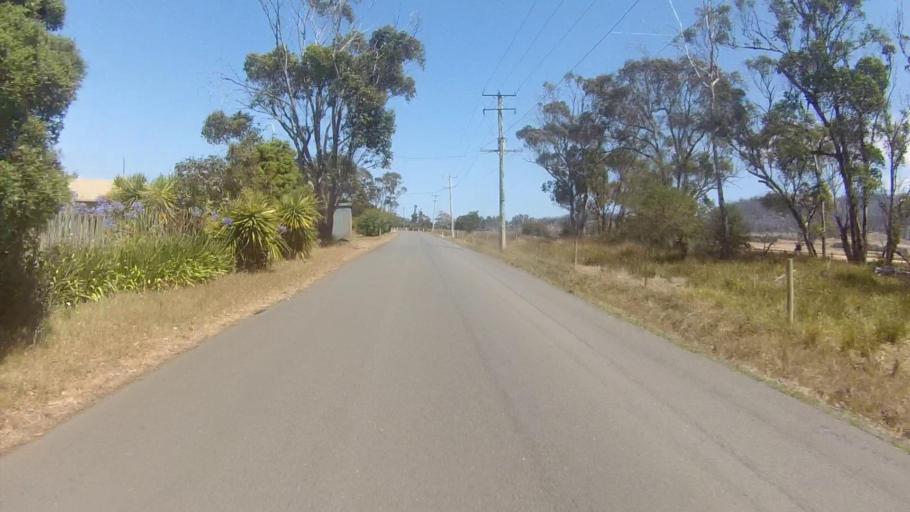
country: AU
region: Tasmania
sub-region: Sorell
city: Sorell
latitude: -42.8609
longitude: 147.8345
